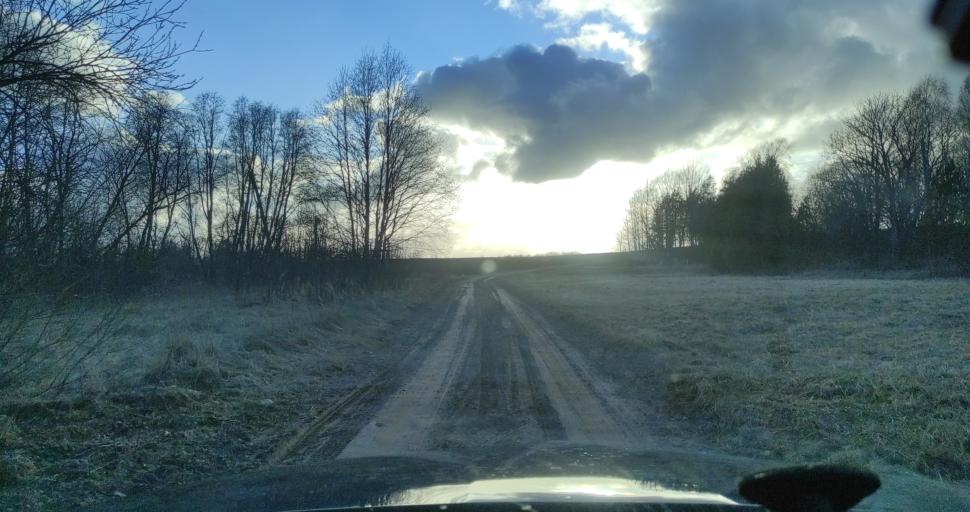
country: LV
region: Aizpute
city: Aizpute
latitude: 56.8466
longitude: 21.7747
